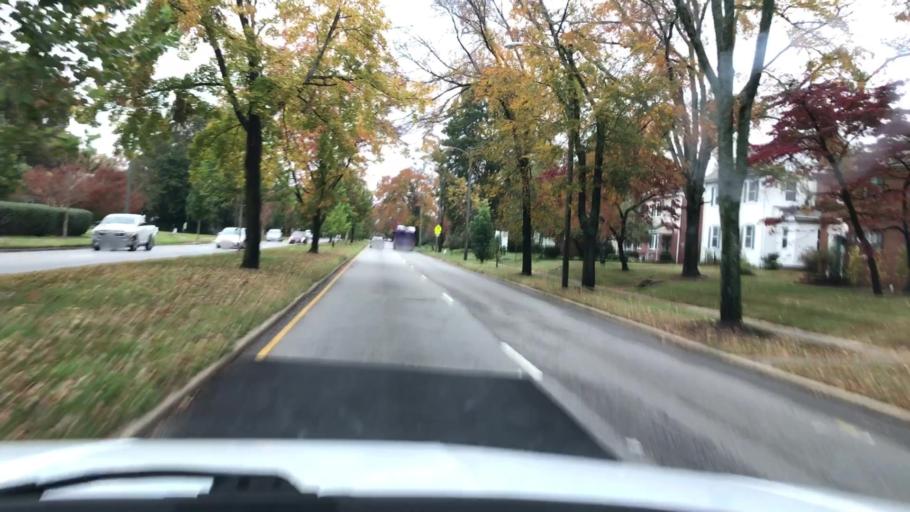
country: US
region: Virginia
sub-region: Henrico County
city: Lakeside
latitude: 37.5924
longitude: -77.4486
